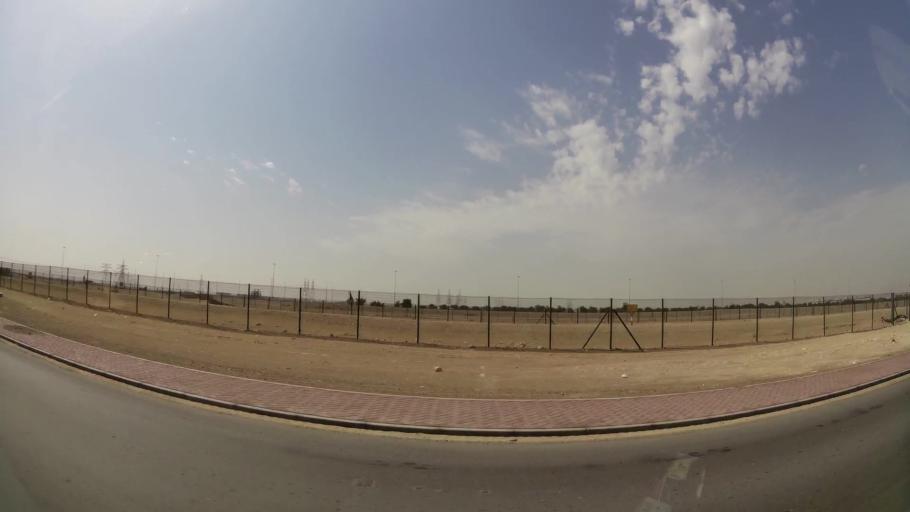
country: AE
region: Abu Dhabi
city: Abu Dhabi
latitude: 24.3138
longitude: 54.5303
